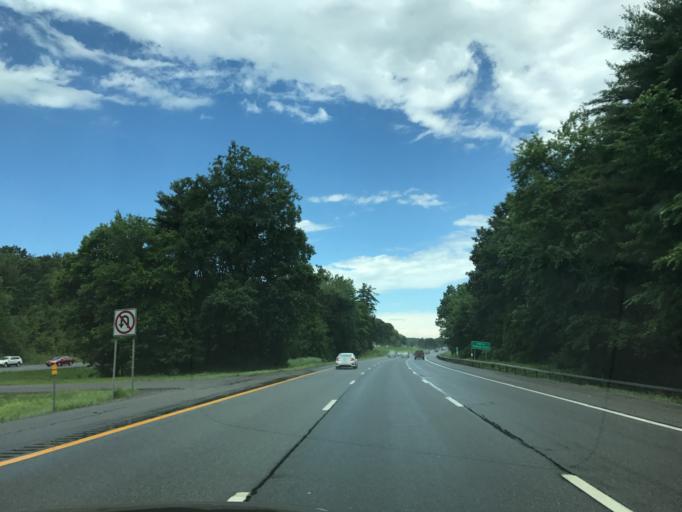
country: US
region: New York
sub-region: Albany County
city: Cohoes
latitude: 42.8260
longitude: -73.7688
